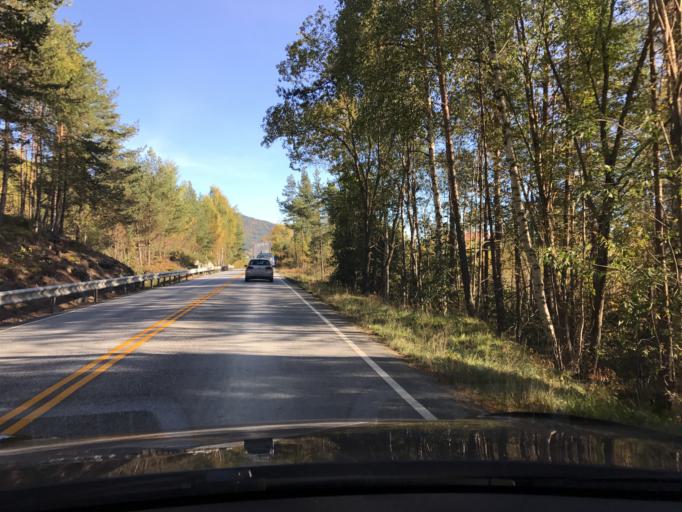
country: NO
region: Sogn og Fjordane
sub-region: Sogndal
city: Sogndalsfjora
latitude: 61.2079
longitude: 7.1849
